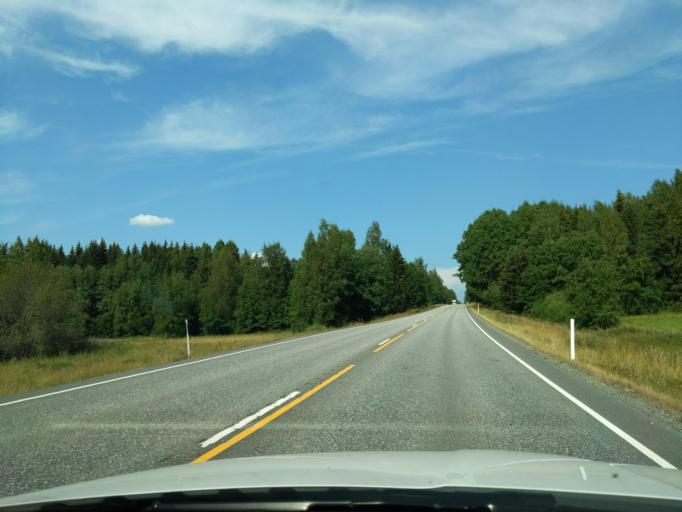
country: FI
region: Paijanne Tavastia
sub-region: Lahti
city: Padasjoki
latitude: 61.4098
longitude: 25.1789
